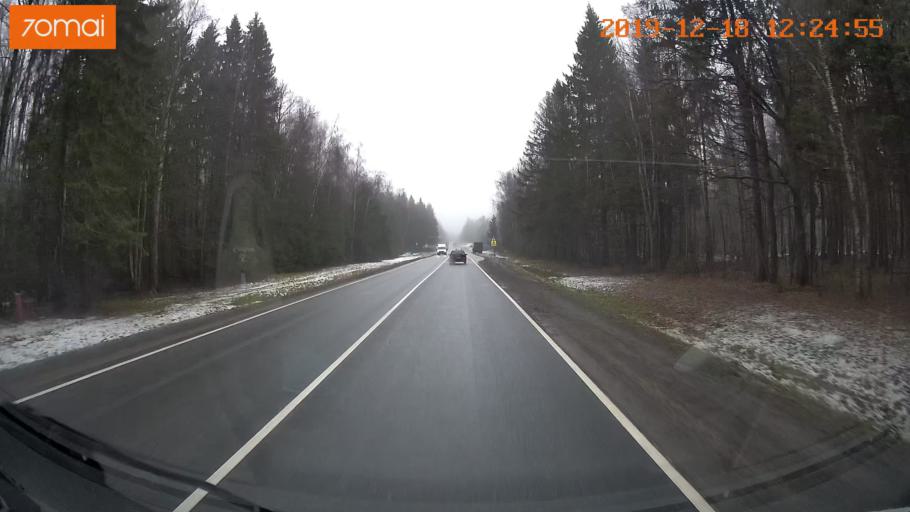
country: RU
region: Moskovskaya
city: Novopetrovskoye
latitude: 56.0311
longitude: 36.5004
